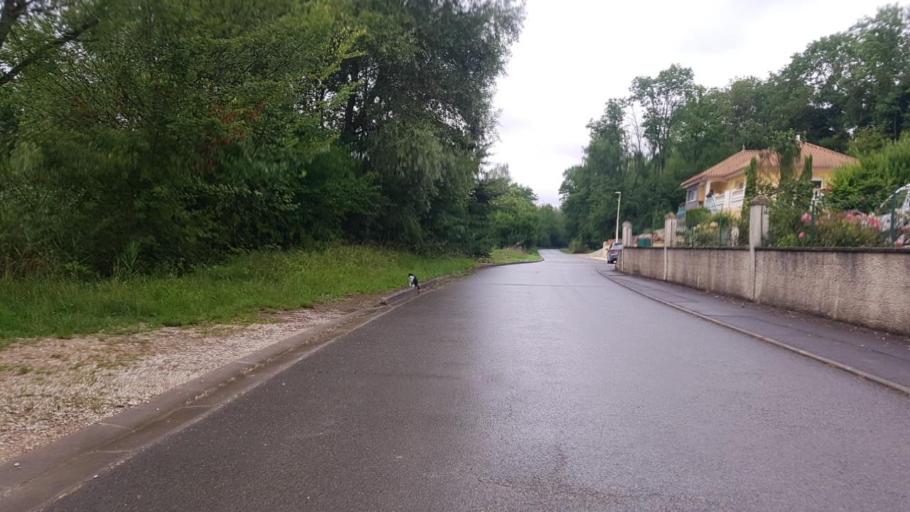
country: FR
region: Champagne-Ardenne
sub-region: Departement de la Marne
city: Vitry-le-Francois
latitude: 48.7514
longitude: 4.5709
